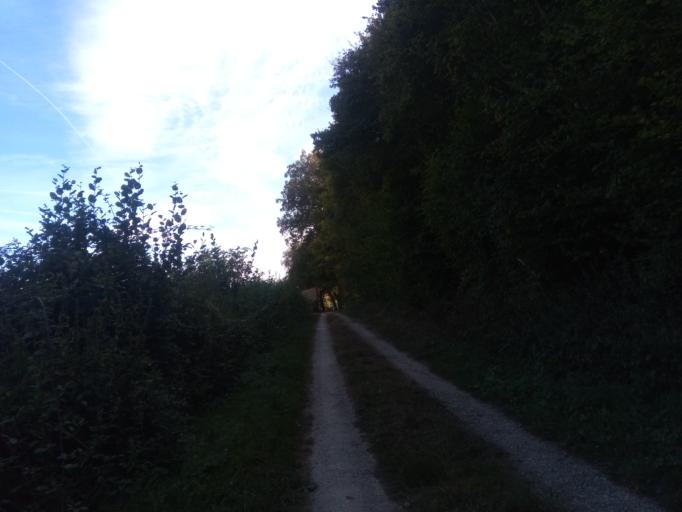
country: FR
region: Poitou-Charentes
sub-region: Departement de la Vienne
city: Saint-Savin
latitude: 46.5572
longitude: 0.8646
